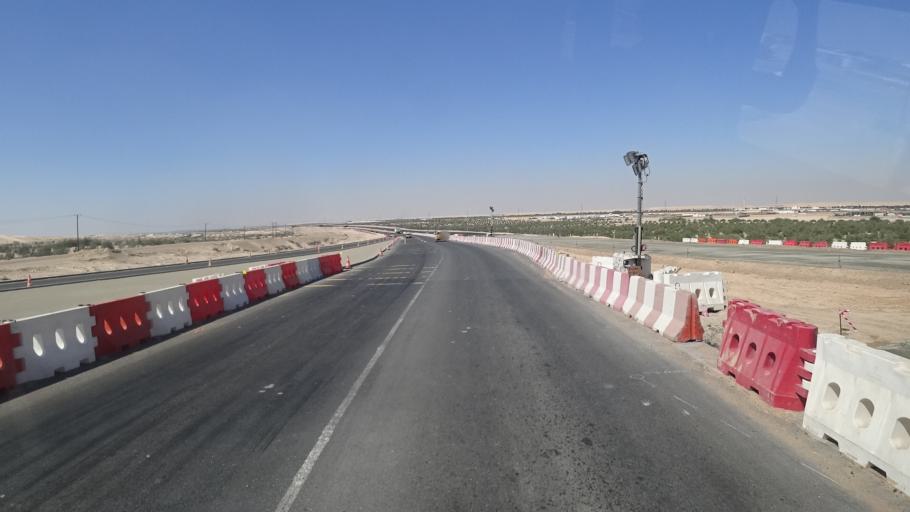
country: AE
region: Abu Dhabi
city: Abu Dhabi
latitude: 24.2021
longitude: 54.8574
